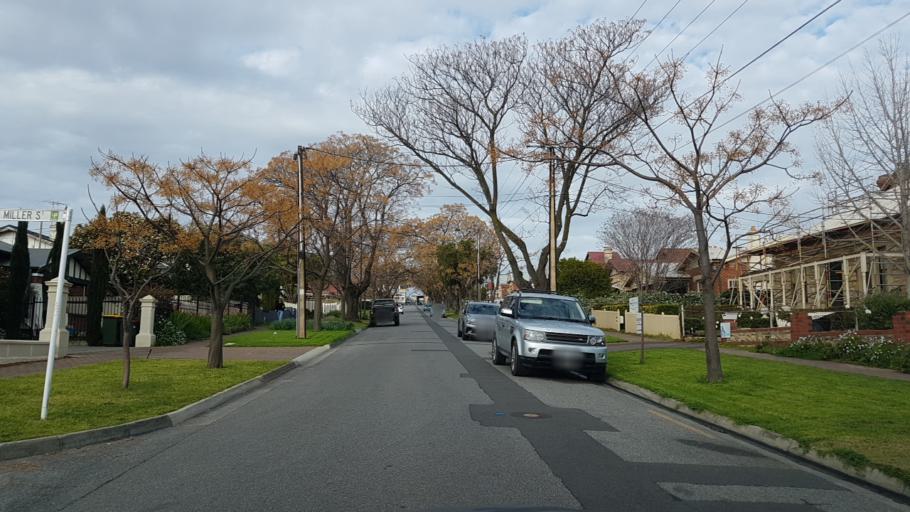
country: AU
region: South Australia
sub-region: Prospect
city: Prospect
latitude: -34.8774
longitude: 138.5905
